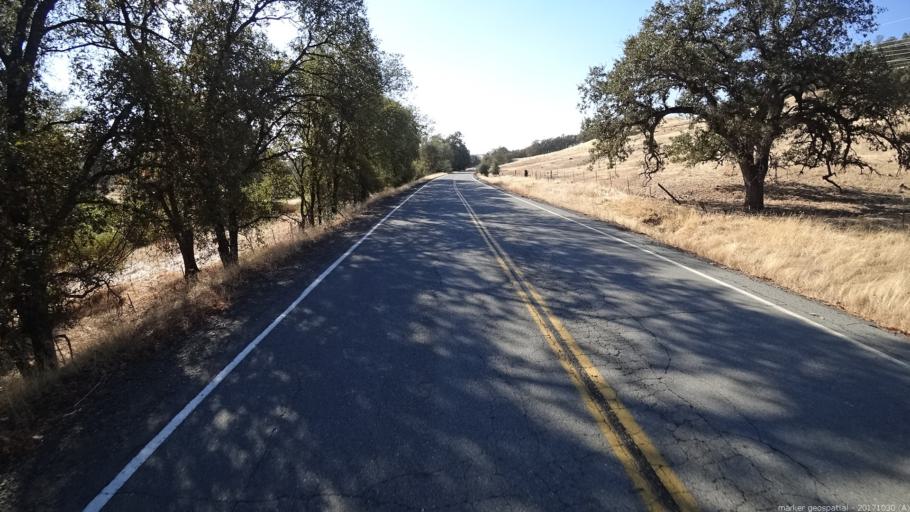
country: US
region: California
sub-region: Shasta County
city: Bella Vista
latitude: 40.6543
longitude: -122.0746
